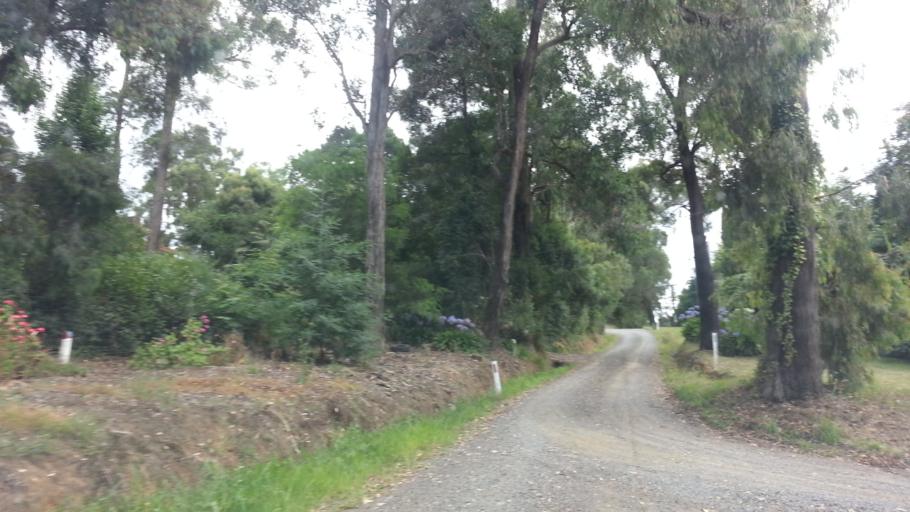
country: AU
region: Victoria
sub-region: Cardinia
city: Emerald
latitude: -37.9388
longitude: 145.4394
